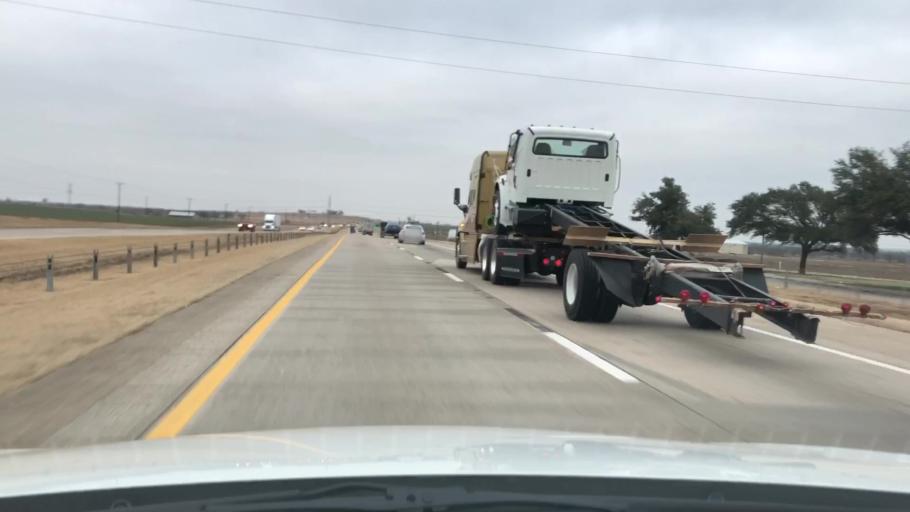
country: US
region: Texas
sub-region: Cooke County
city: Gainesville
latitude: 33.5277
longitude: -97.1664
